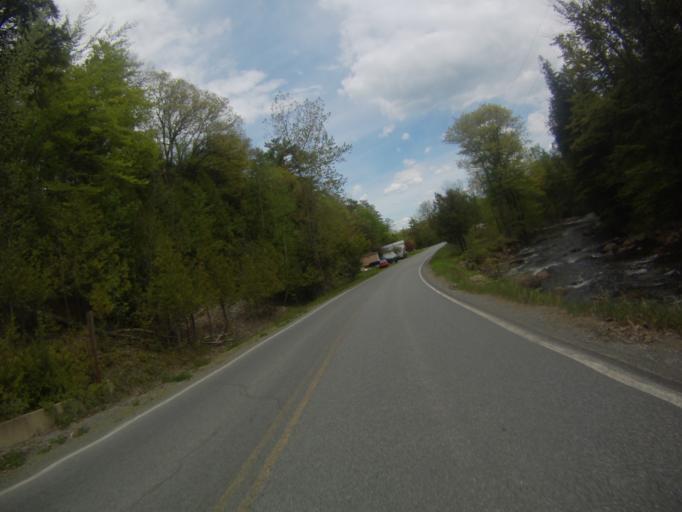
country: US
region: New York
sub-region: Essex County
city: Ticonderoga
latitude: 43.9421
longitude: -73.4748
